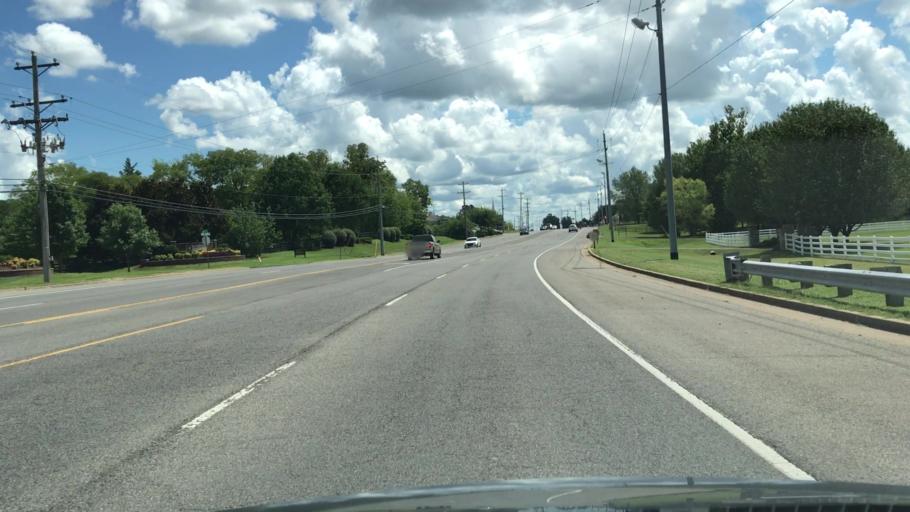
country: US
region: Tennessee
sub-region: Rutherford County
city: Murfreesboro
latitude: 35.8448
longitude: -86.4595
